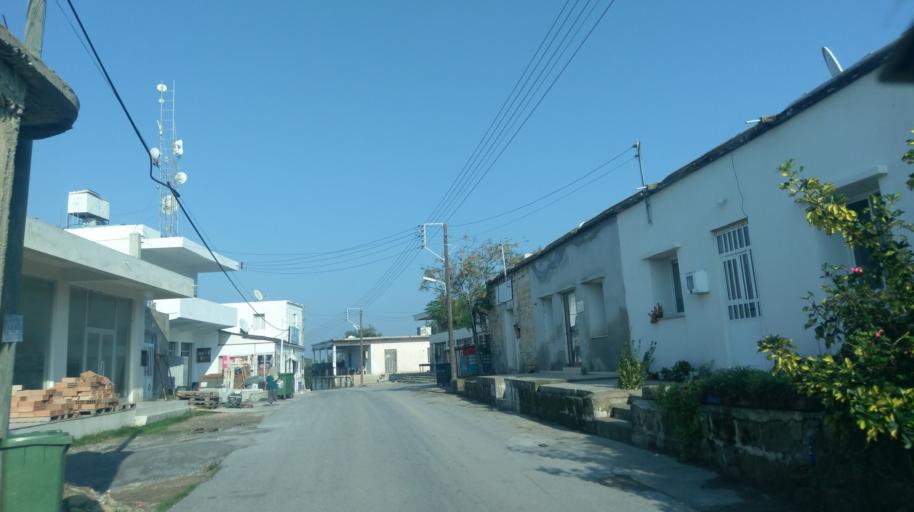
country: CY
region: Ammochostos
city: Leonarisso
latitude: 35.5394
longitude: 34.2160
